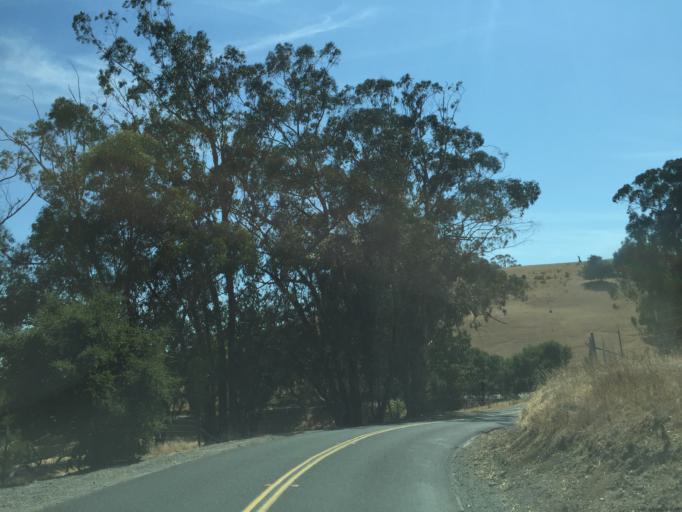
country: US
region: California
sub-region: Solano County
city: Benicia
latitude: 38.0270
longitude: -122.1868
